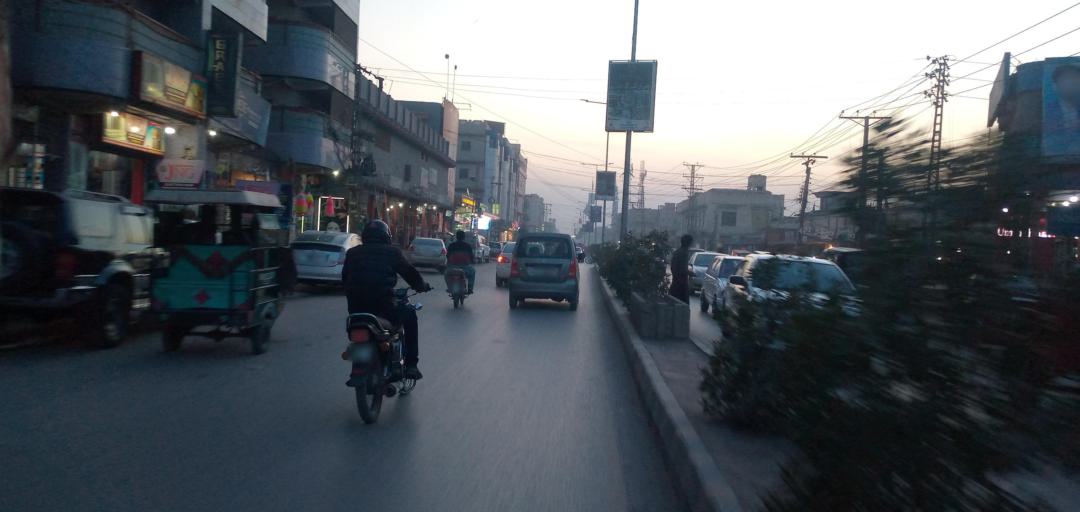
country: PK
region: Khyber Pakhtunkhwa
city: Peshawar
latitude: 34.0275
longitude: 71.5991
